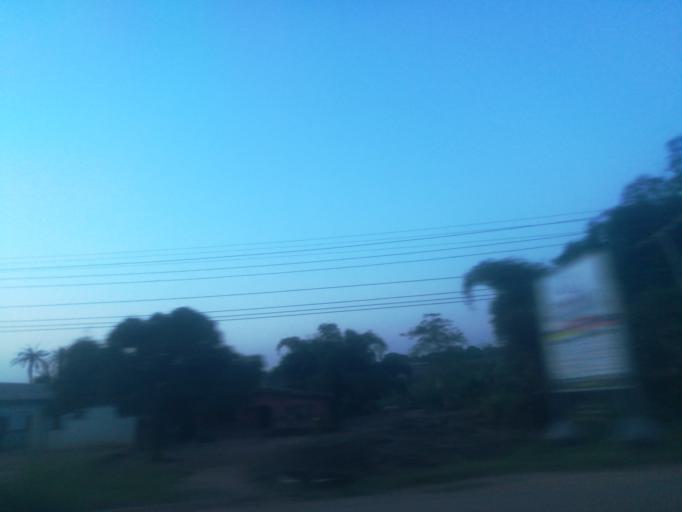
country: NG
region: Ogun
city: Abeokuta
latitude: 7.1855
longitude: 3.4304
